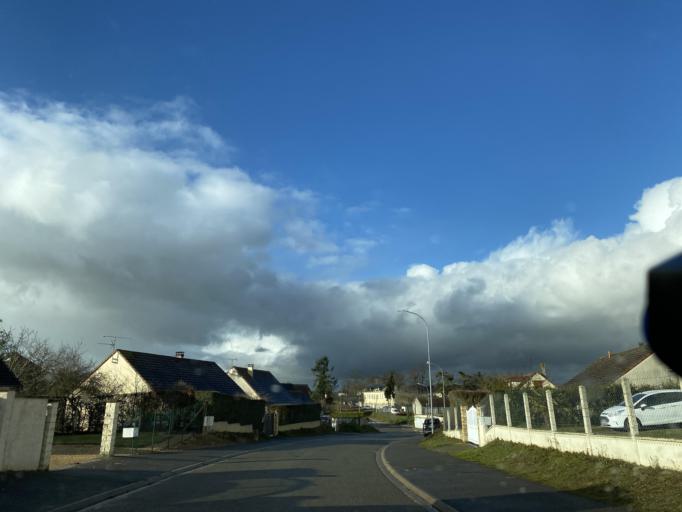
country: FR
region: Centre
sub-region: Departement d'Eure-et-Loir
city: Brezolles
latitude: 48.6909
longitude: 1.0783
